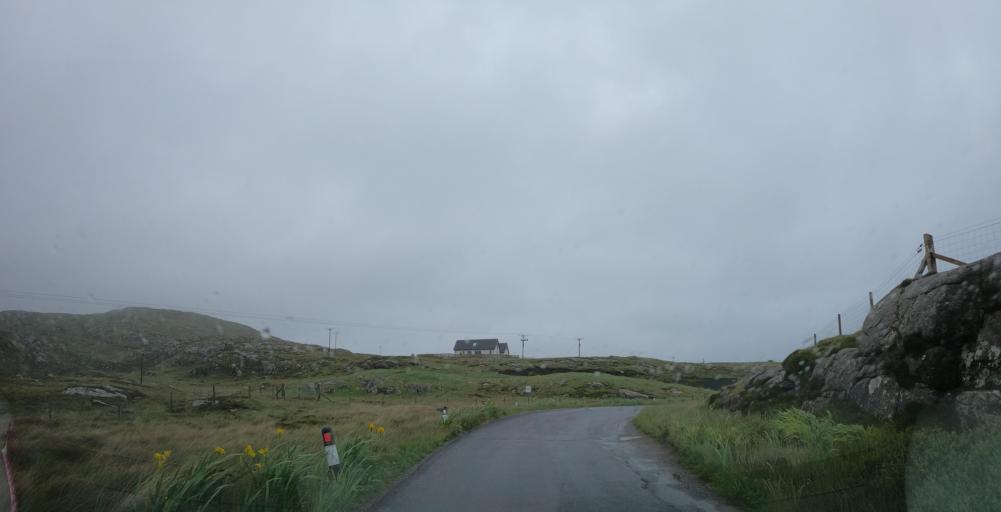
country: GB
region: Scotland
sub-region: Eilean Siar
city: Barra
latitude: 57.0081
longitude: -7.4296
